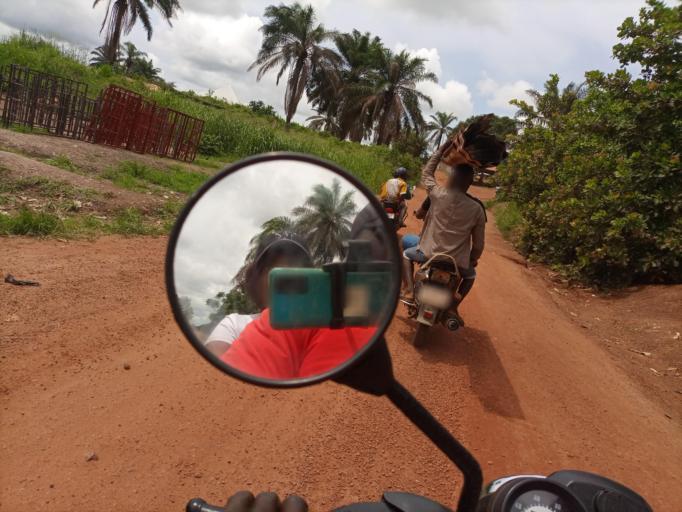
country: SL
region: Southern Province
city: Baoma
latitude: 7.9718
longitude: -11.7171
